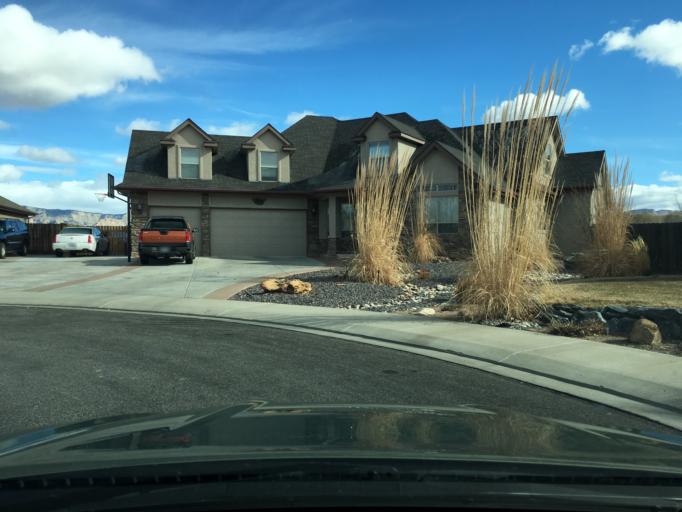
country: US
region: Colorado
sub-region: Mesa County
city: Grand Junction
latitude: 39.1307
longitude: -108.5535
